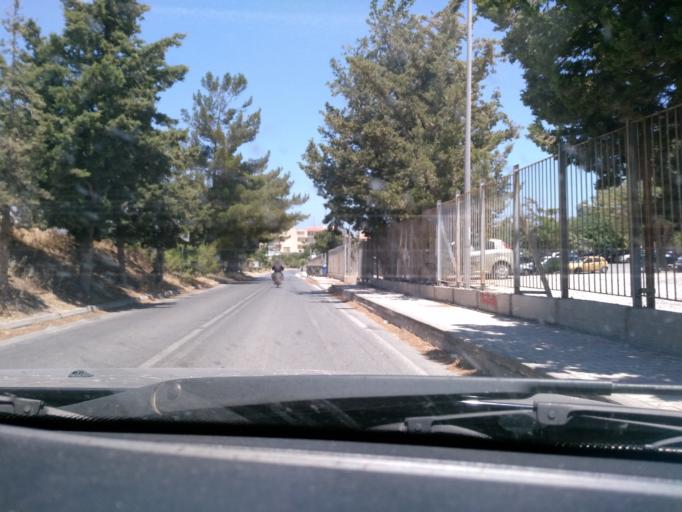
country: GR
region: Crete
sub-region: Nomos Irakleiou
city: Gazi
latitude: 35.3177
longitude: 25.1012
